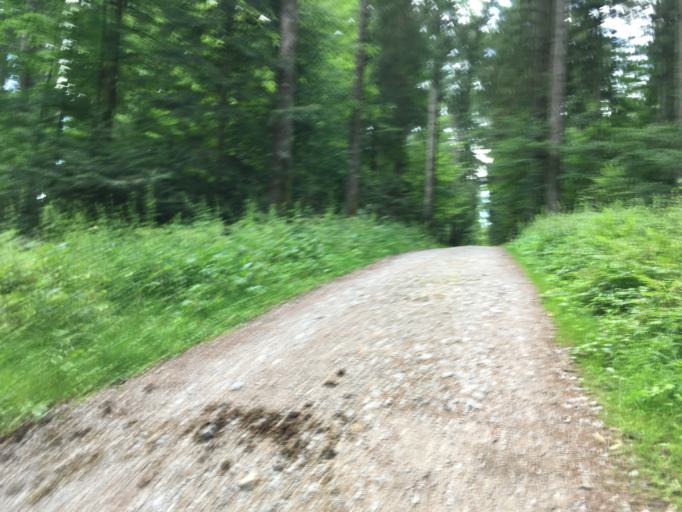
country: DE
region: Baden-Wuerttemberg
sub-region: Karlsruhe Region
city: Freudenstadt
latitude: 48.4380
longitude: 8.4064
